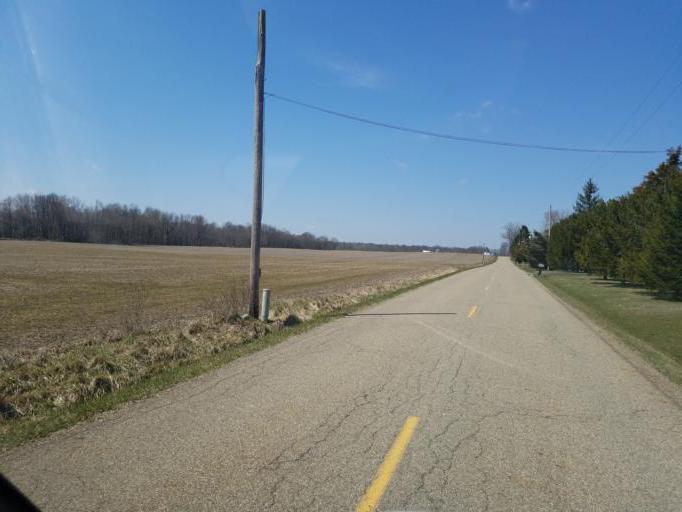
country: US
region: Ohio
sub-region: Knox County
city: Centerburg
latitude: 40.2911
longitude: -82.6352
